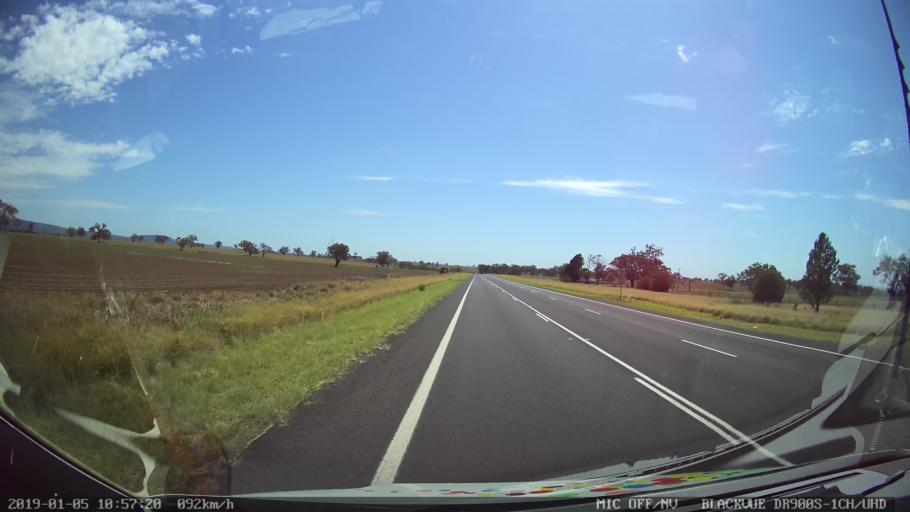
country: AU
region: New South Wales
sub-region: Warrumbungle Shire
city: Coonabarabran
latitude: -31.4322
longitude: 149.1682
